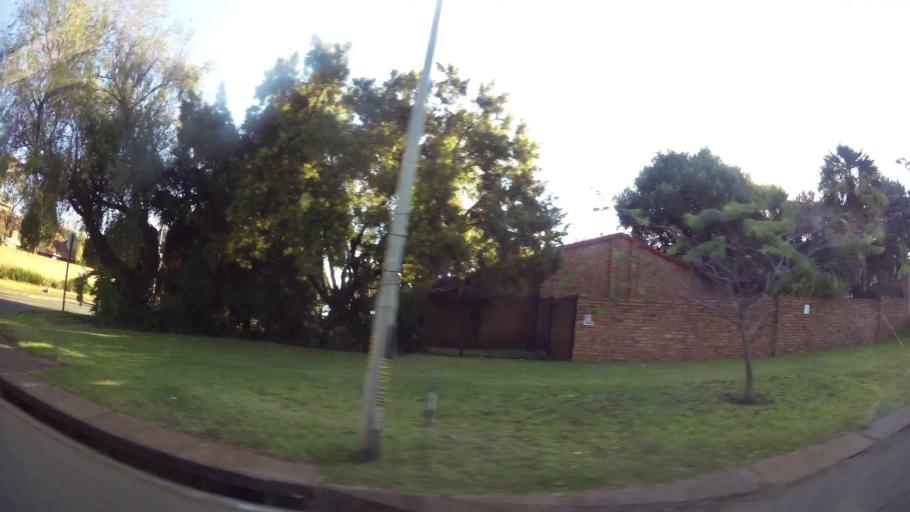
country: ZA
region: Gauteng
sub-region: City of Tshwane Metropolitan Municipality
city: Centurion
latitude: -25.8554
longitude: 28.1577
